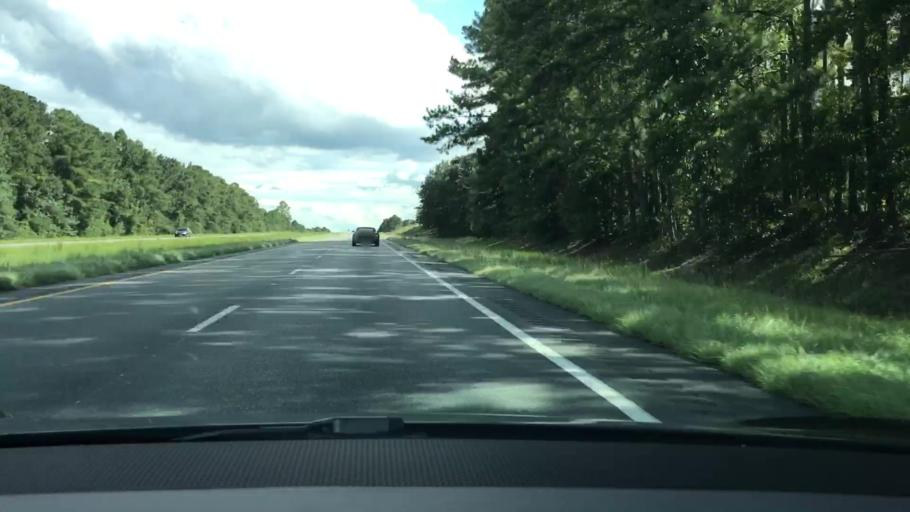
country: US
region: Alabama
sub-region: Pike County
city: Troy
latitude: 31.9057
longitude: -86.0117
